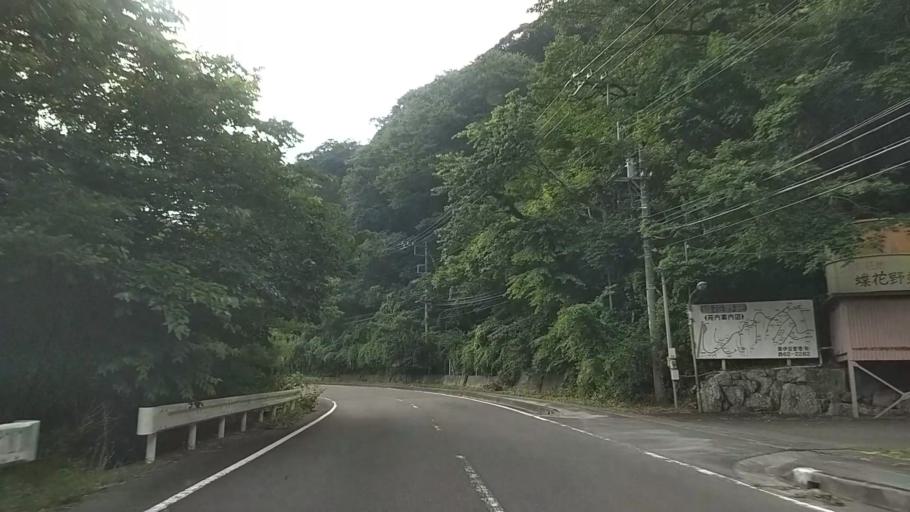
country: JP
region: Shizuoka
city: Shimoda
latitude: 34.6516
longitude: 138.8280
